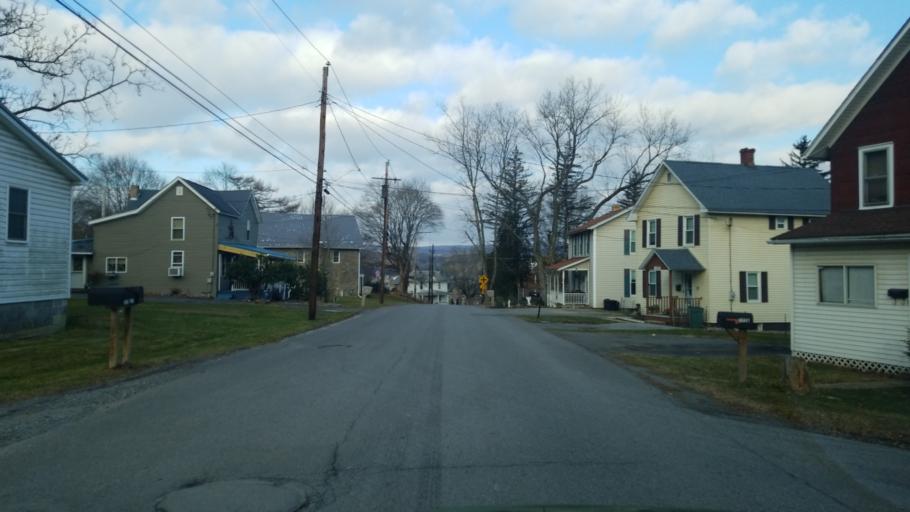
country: US
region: Pennsylvania
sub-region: Clearfield County
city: Clearfield
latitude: 41.0185
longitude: -78.4306
